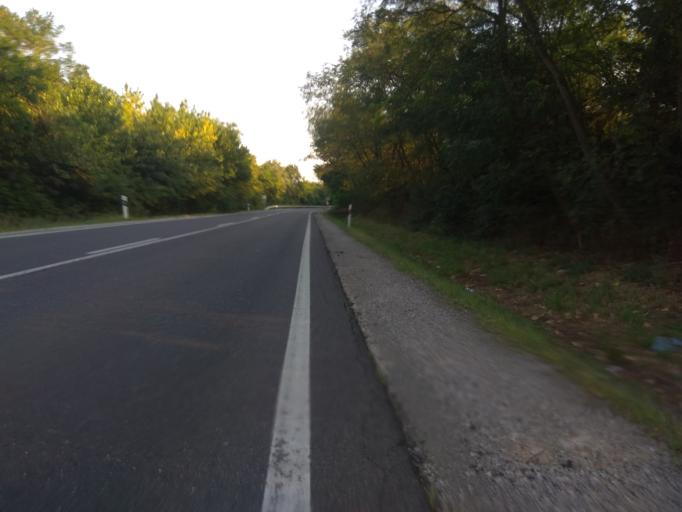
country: HU
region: Borsod-Abauj-Zemplen
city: Nyekladhaza
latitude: 47.9604
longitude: 20.8345
